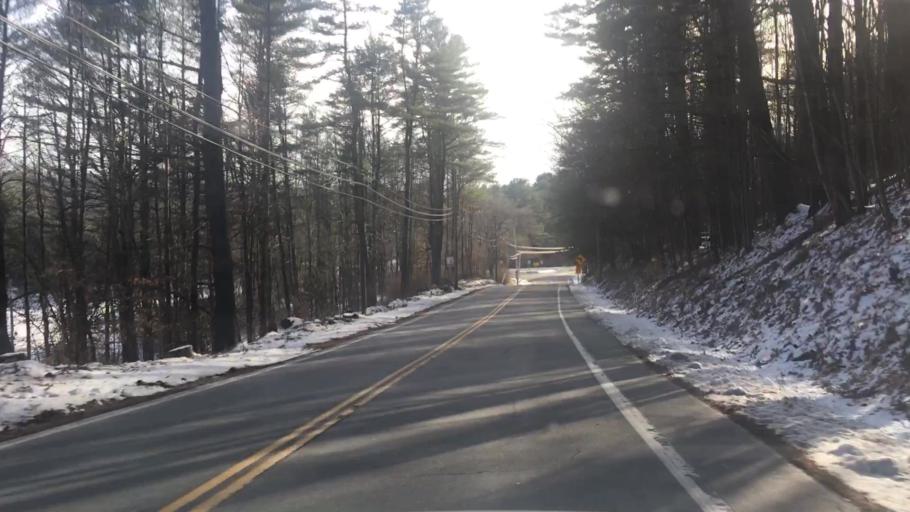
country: US
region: New Hampshire
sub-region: Merrimack County
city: Canterbury
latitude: 43.3038
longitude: -71.5666
